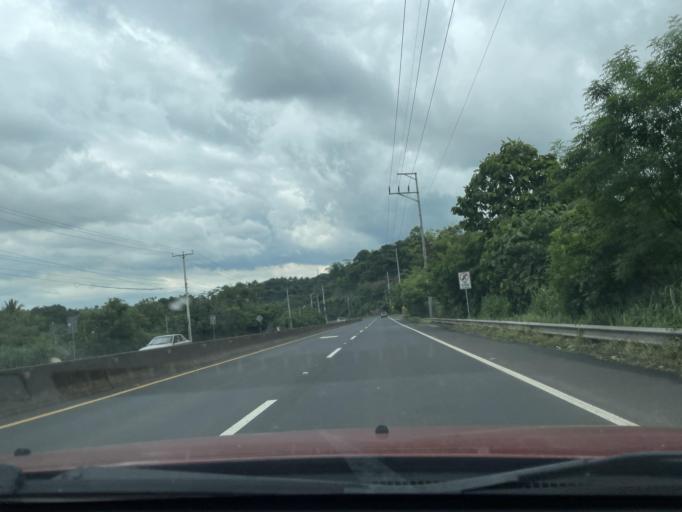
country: SV
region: Sonsonate
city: Armenia
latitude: 13.7501
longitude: -89.4961
